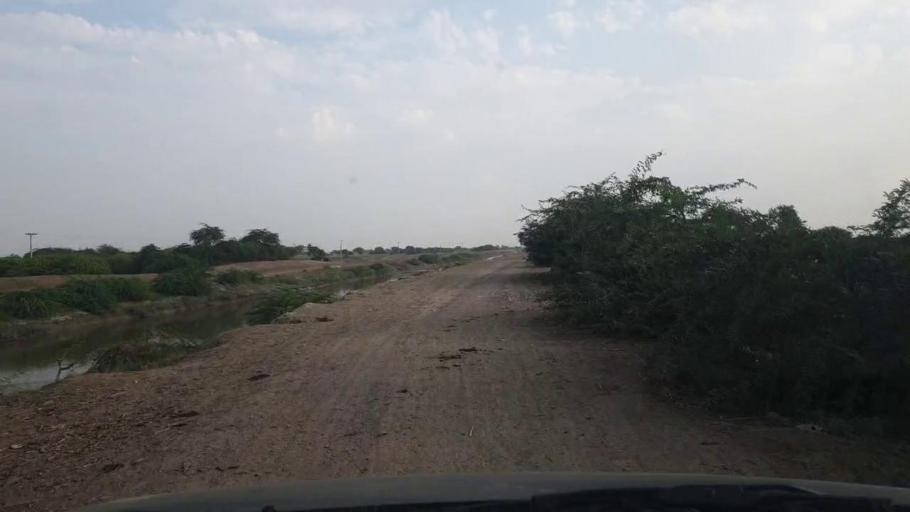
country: PK
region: Sindh
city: Badin
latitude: 24.5285
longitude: 68.6792
